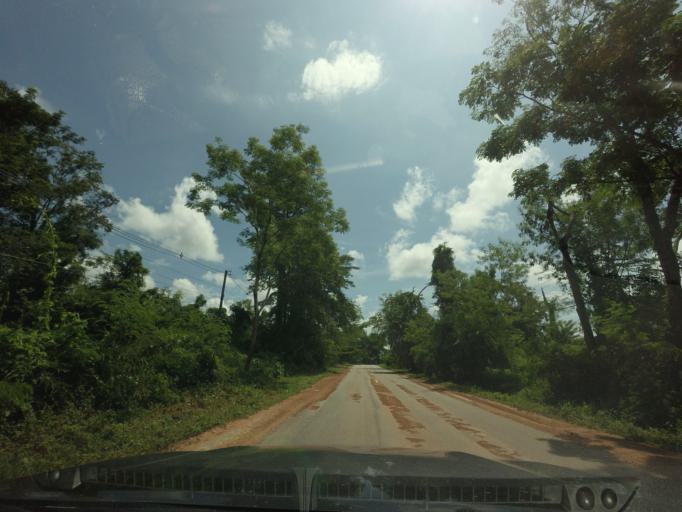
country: TH
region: Nong Khai
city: Pho Tak
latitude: 17.7853
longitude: 102.3713
